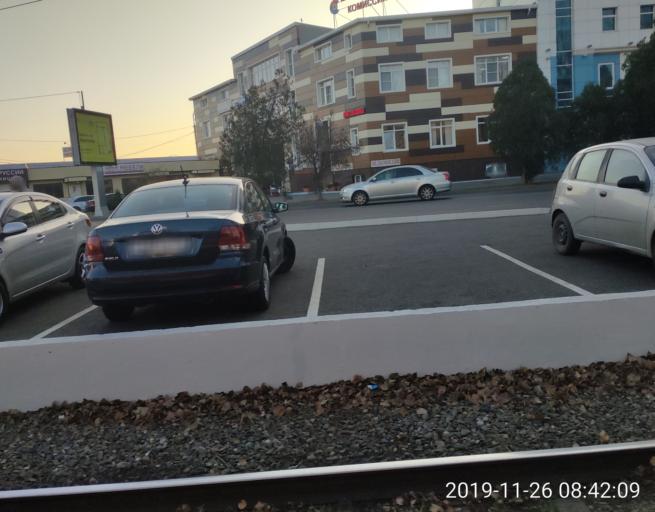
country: RU
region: Krasnodarskiy
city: Krasnodar
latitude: 45.0521
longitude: 38.9848
